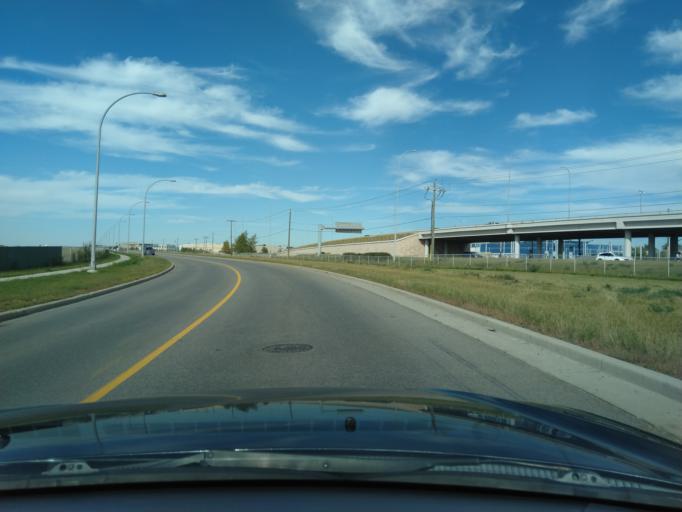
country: CA
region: Alberta
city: Calgary
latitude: 51.1017
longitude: -113.9829
